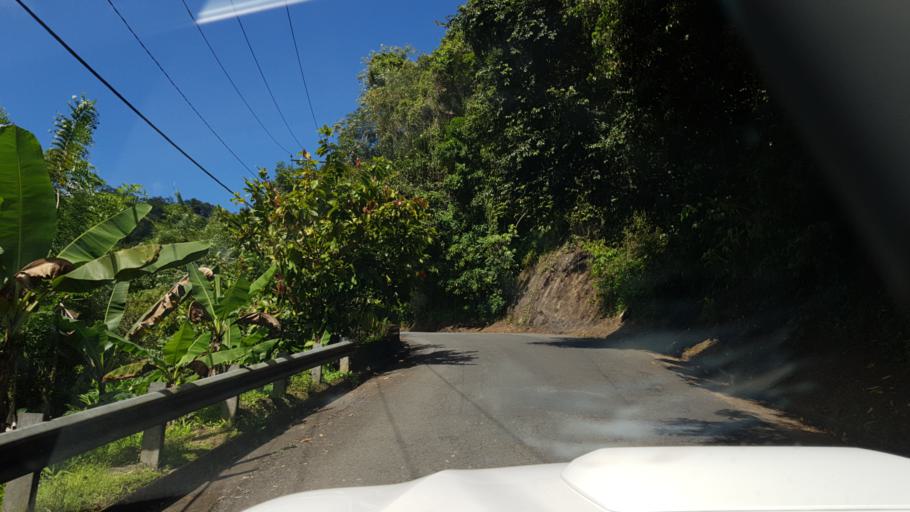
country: LC
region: Castries Quarter
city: Castries
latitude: 13.9906
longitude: -60.9737
